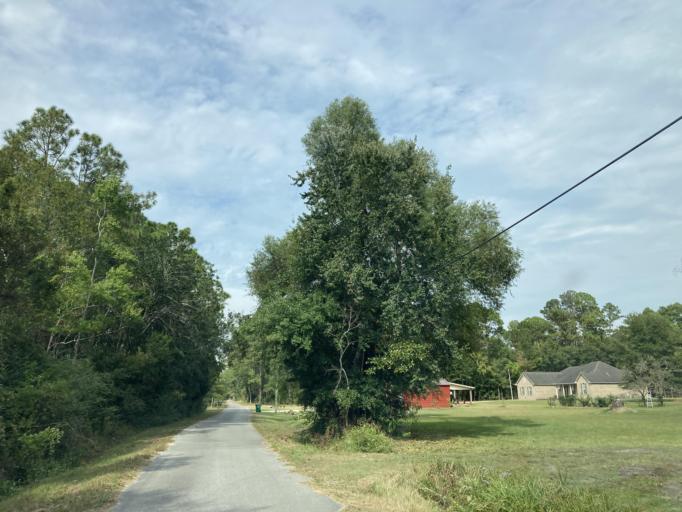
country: US
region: Mississippi
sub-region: Jackson County
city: Saint Martin
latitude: 30.4672
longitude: -88.8561
